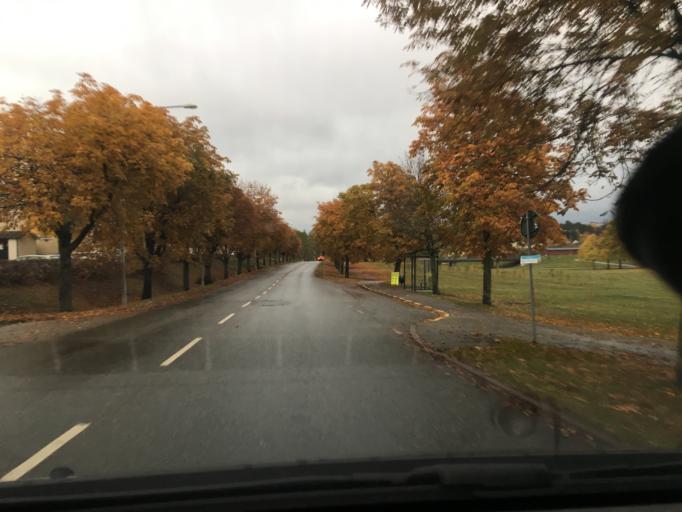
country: SE
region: Stockholm
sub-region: Stockholms Kommun
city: Kista
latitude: 59.3893
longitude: 17.9063
